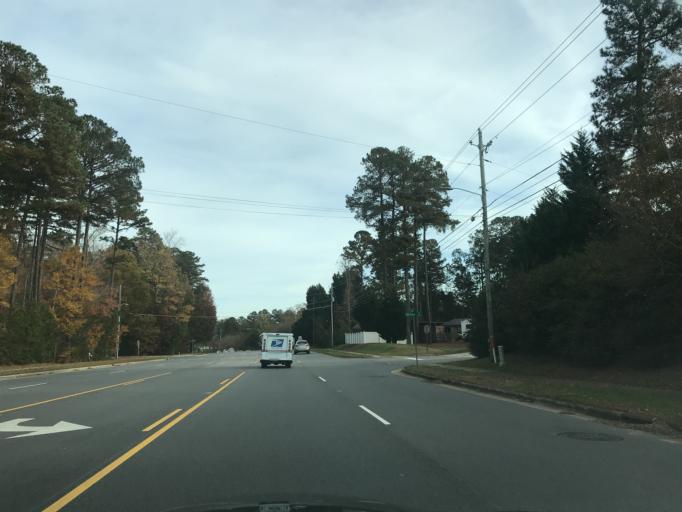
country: US
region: North Carolina
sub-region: Wake County
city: West Raleigh
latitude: 35.8960
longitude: -78.6429
